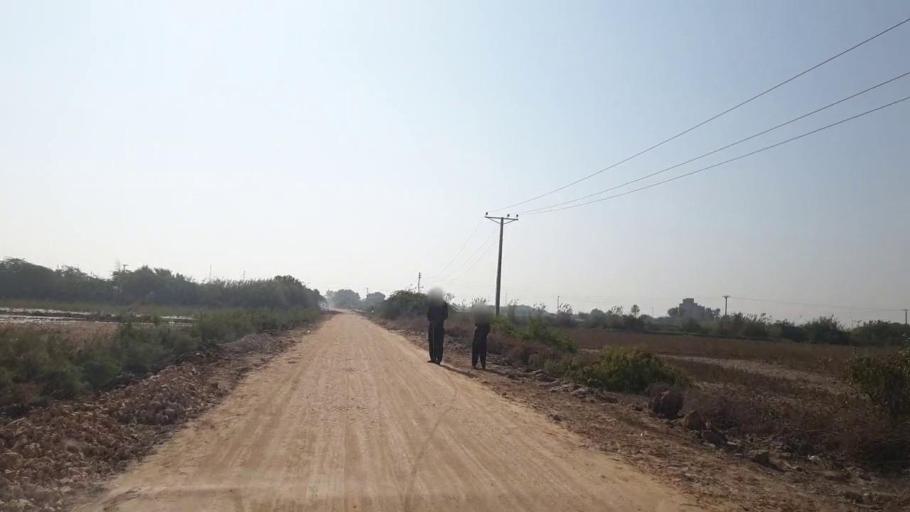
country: PK
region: Sindh
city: Thatta
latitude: 24.7615
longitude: 67.9156
